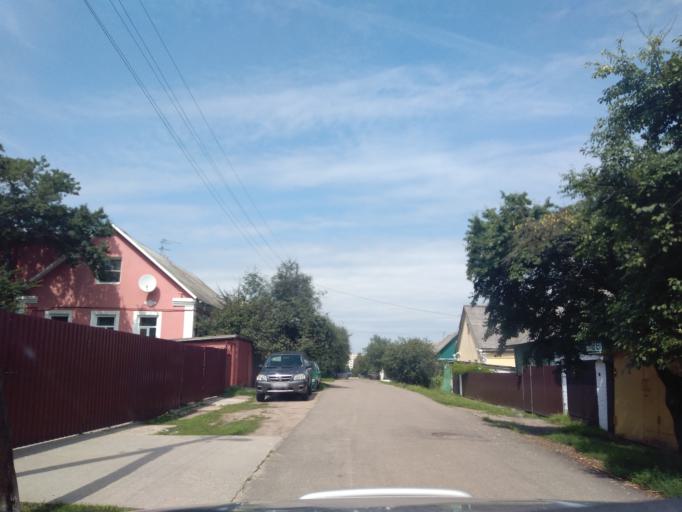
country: BY
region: Minsk
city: Novoye Medvezhino
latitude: 53.8827
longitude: 27.5005
